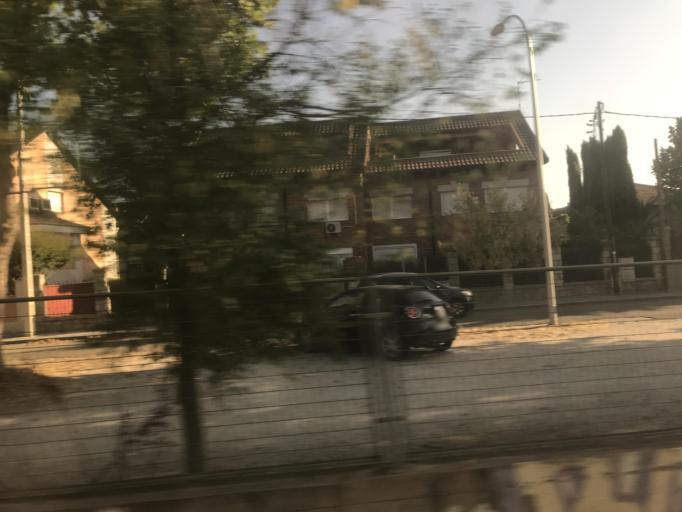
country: ES
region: Madrid
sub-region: Provincia de Madrid
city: Majadahonda
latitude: 40.4727
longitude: -3.8365
